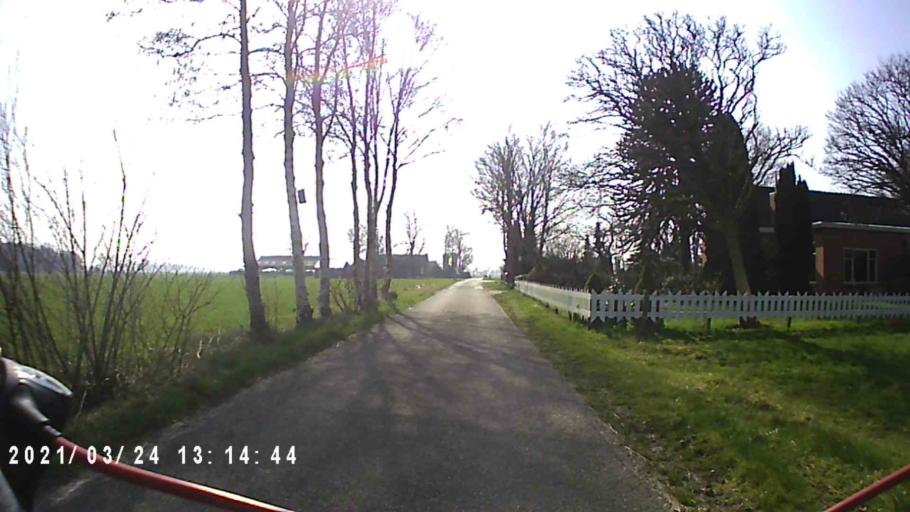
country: NL
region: Groningen
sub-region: Gemeente Leek
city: Leek
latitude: 53.1160
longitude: 6.2929
